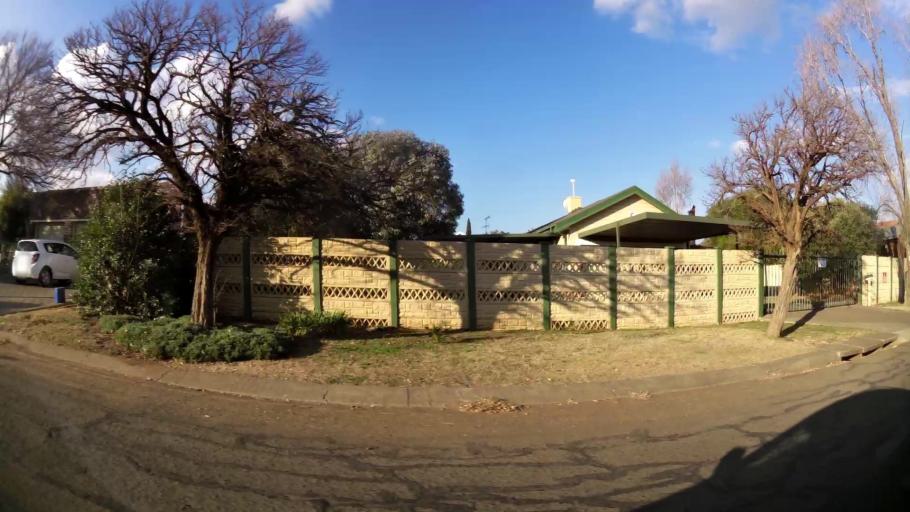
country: ZA
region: Orange Free State
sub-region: Mangaung Metropolitan Municipality
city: Bloemfontein
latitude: -29.1540
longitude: 26.1763
